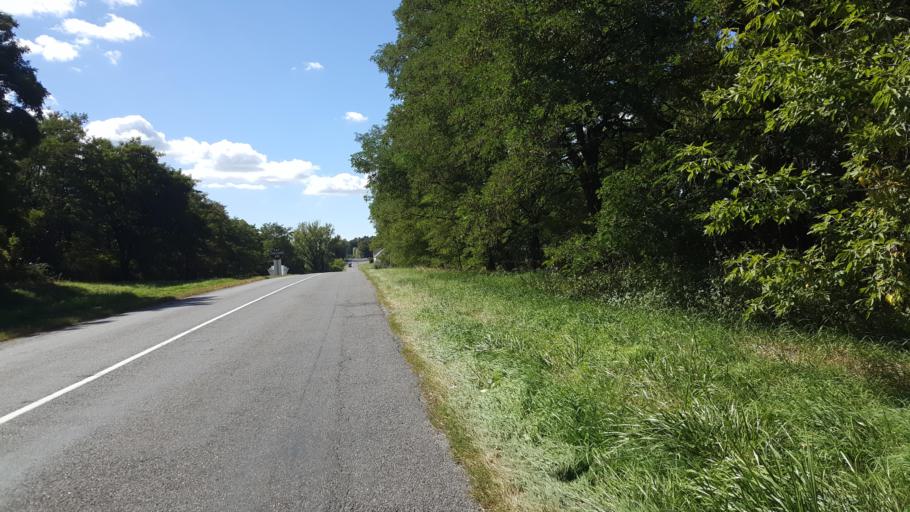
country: BY
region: Brest
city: Vysokaye
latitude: 52.3516
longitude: 23.3498
